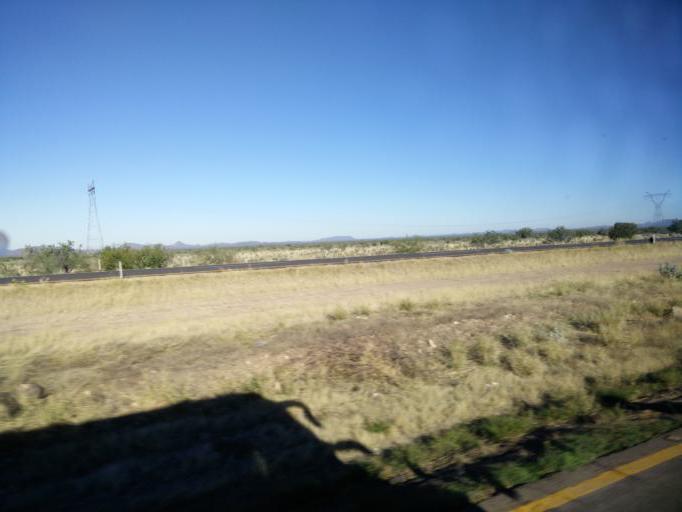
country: MX
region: Sonora
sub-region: Hermosillo
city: Miguel Aleman (La Doce)
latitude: 28.5426
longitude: -111.0416
